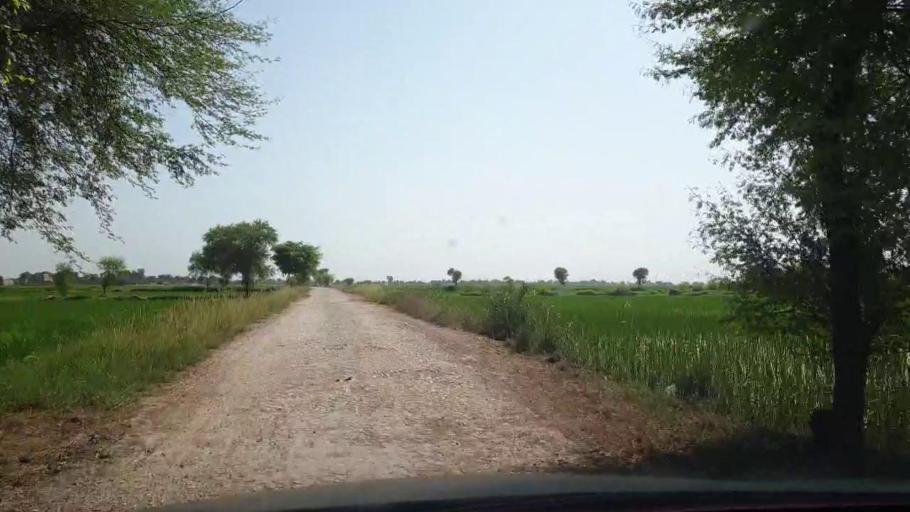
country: PK
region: Sindh
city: Nasirabad
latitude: 27.3637
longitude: 67.8519
